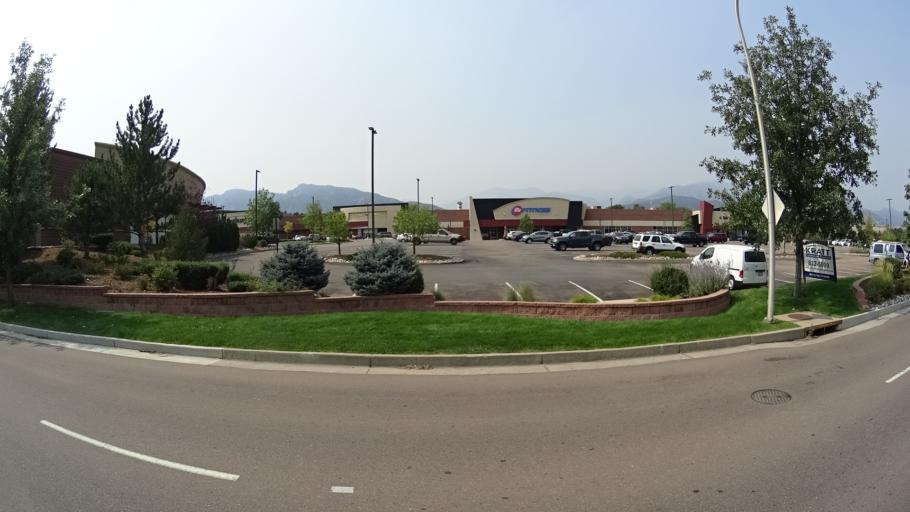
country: US
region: Colorado
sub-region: El Paso County
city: Colorado Springs
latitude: 38.8053
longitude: -104.8199
